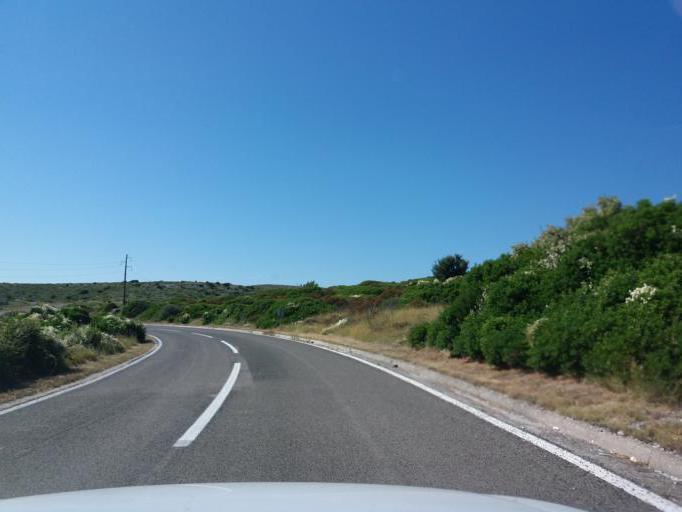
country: HR
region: Zadarska
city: Ugljan
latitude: 44.0302
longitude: 15.0265
